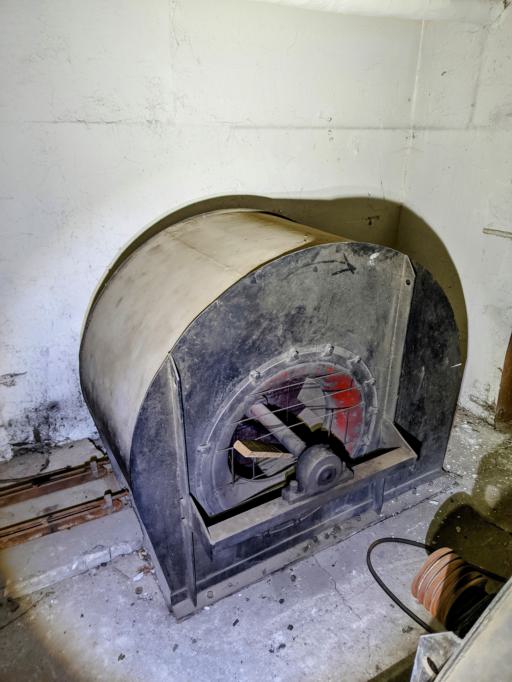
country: PL
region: Lubusz
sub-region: Zielona Gora
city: Zielona Gora
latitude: 51.9792
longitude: 15.4854
